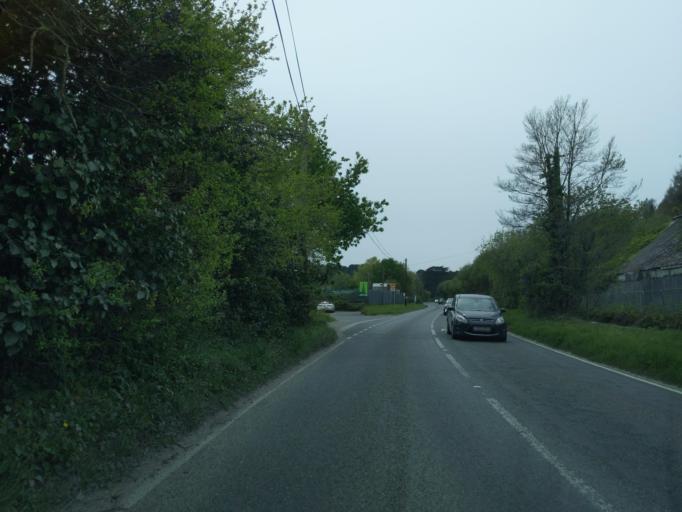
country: GB
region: England
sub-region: Cornwall
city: Par
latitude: 50.3447
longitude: -4.7084
